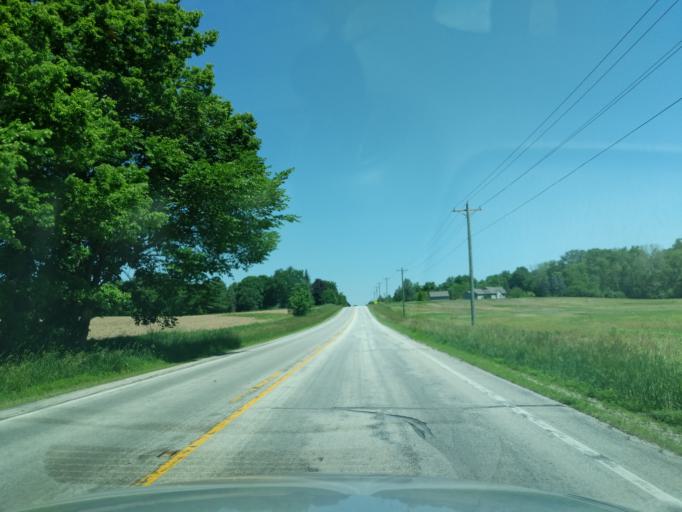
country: US
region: Indiana
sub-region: Whitley County
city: Columbia City
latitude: 41.1959
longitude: -85.4916
